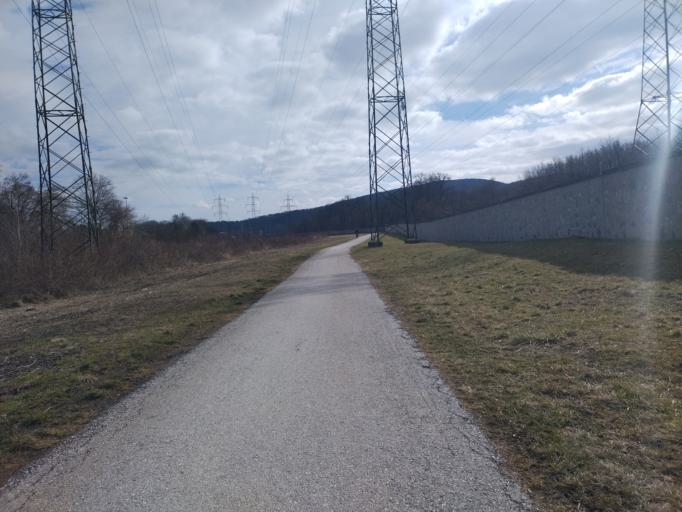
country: AT
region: Lower Austria
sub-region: Politischer Bezirk Wien-Umgebung
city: Purkersdorf
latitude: 48.2029
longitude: 16.2236
